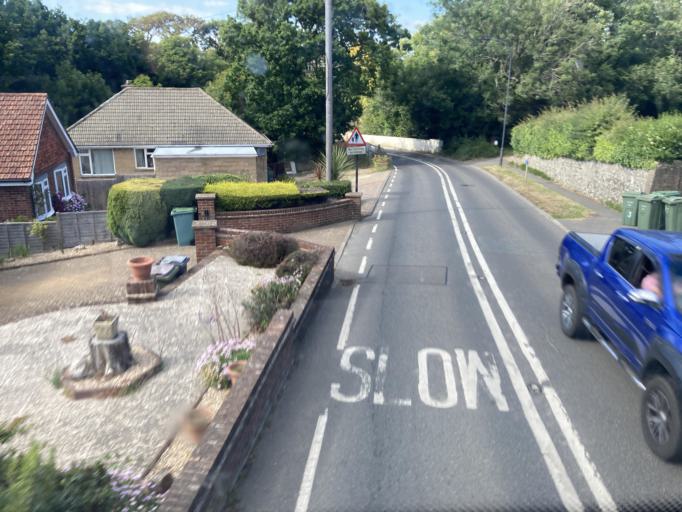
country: GB
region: England
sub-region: Isle of Wight
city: Shanklin
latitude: 50.6291
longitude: -1.1972
